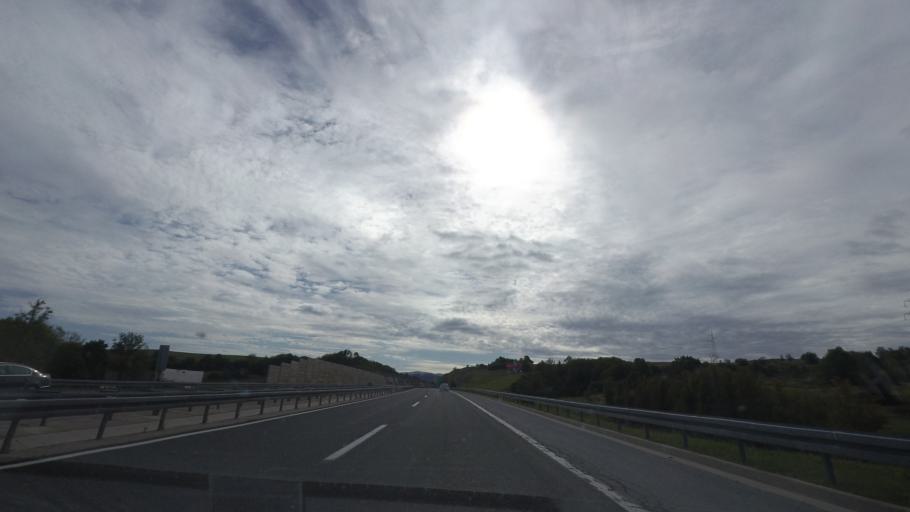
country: HR
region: Licko-Senjska
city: Brinje
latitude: 45.0243
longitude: 15.1556
